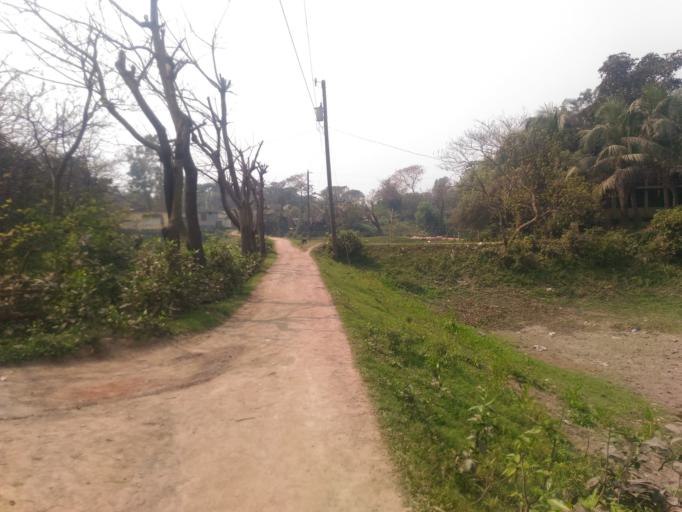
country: BD
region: Dhaka
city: Narayanganj
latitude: 23.6403
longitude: 90.4386
